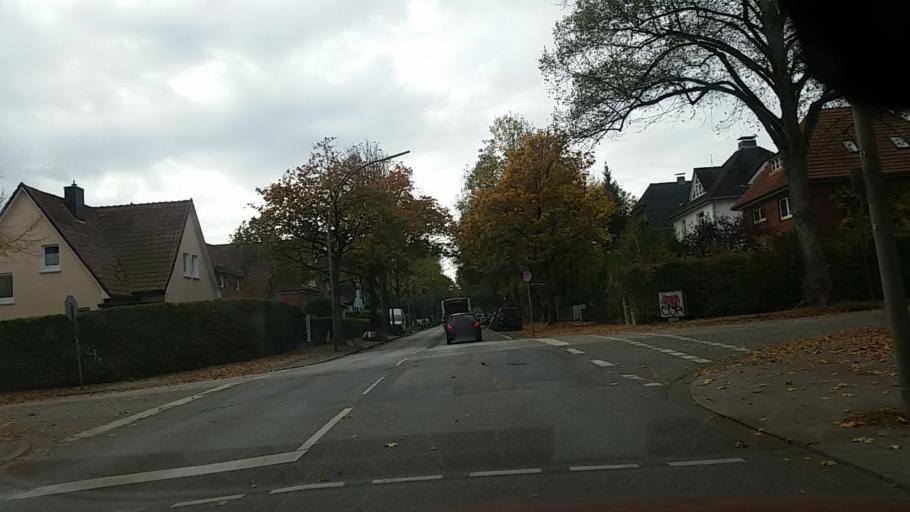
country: DE
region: Hamburg
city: Ohlsdorf
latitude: 53.6355
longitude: 10.0325
